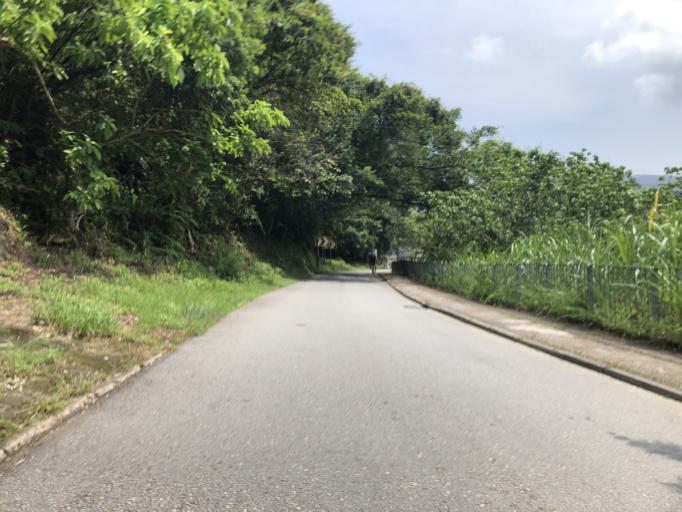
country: CN
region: Guangdong
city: Haishan
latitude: 22.5249
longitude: 114.2104
